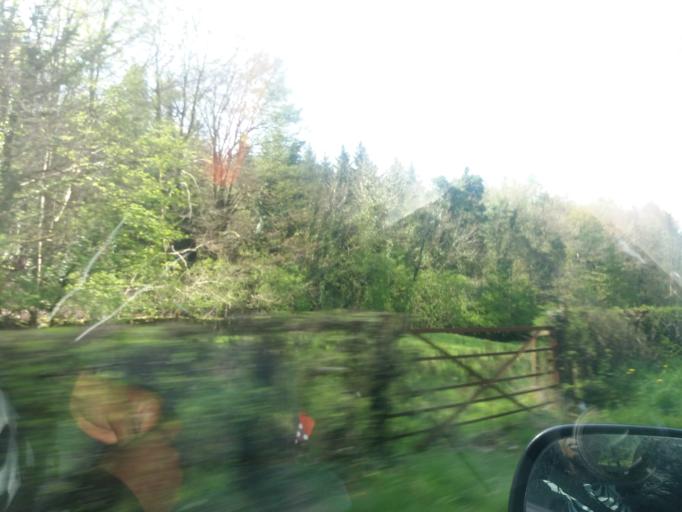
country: GB
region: Northern Ireland
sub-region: Fermanagh District
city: Enniskillen
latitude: 54.3818
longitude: -7.6923
